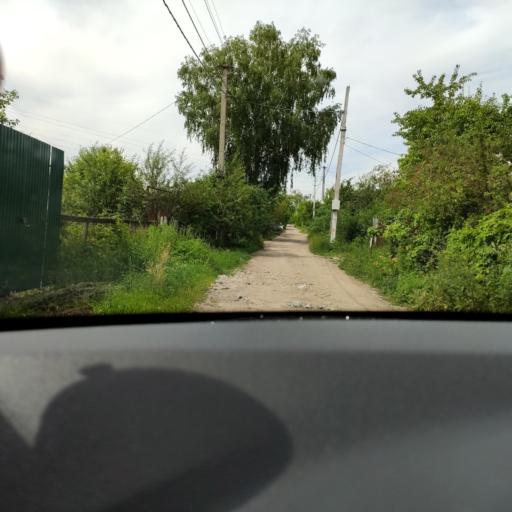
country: RU
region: Samara
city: Petra-Dubrava
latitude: 53.2829
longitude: 50.2872
